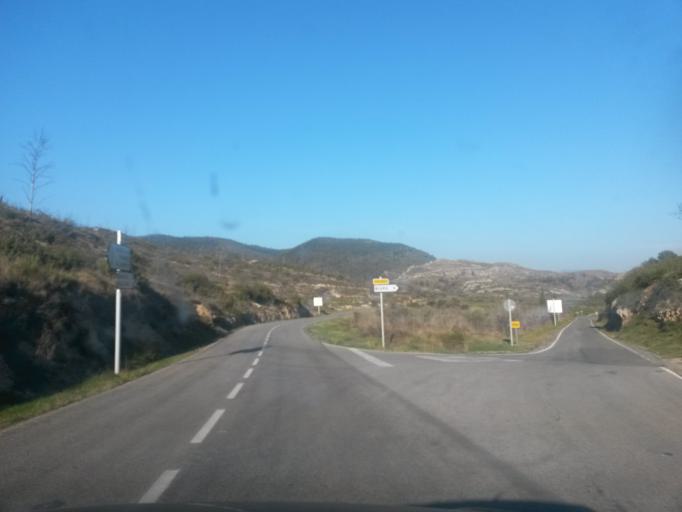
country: ES
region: Catalonia
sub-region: Provincia de Girona
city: Biure
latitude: 42.3381
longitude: 2.8724
